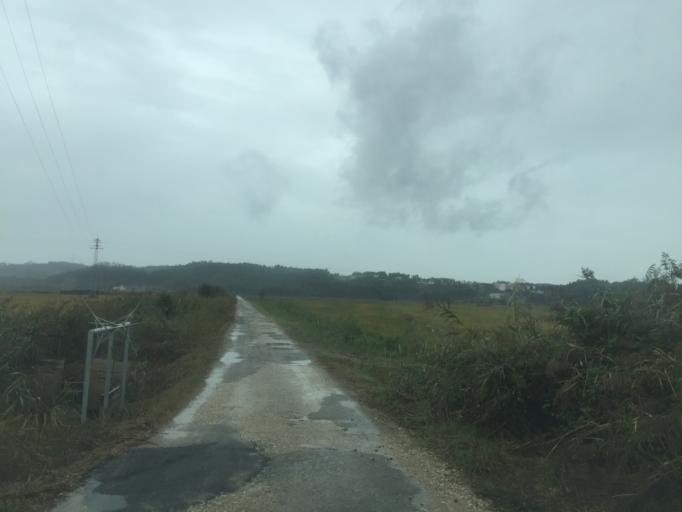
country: PT
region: Coimbra
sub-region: Figueira da Foz
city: Lavos
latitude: 40.1025
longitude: -8.8061
